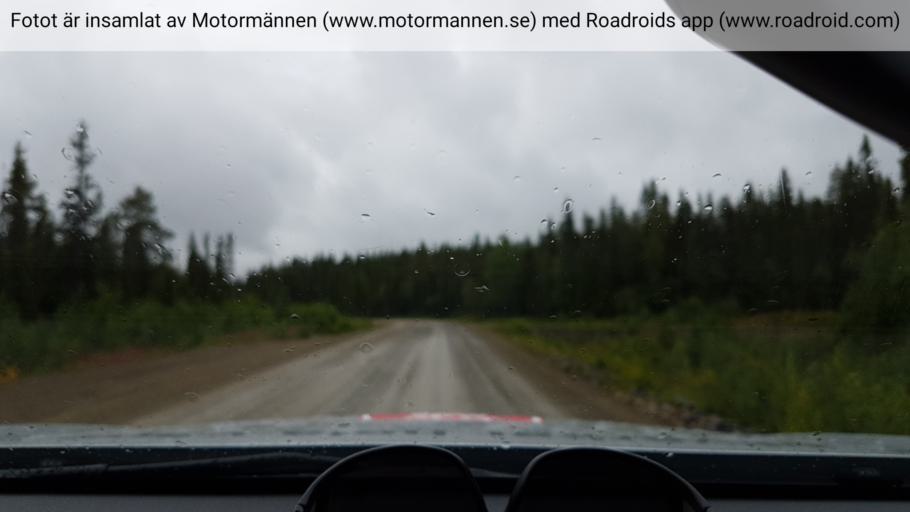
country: SE
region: Vaesterbotten
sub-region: Lycksele Kommun
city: Soderfors
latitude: 64.7788
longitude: 17.6497
